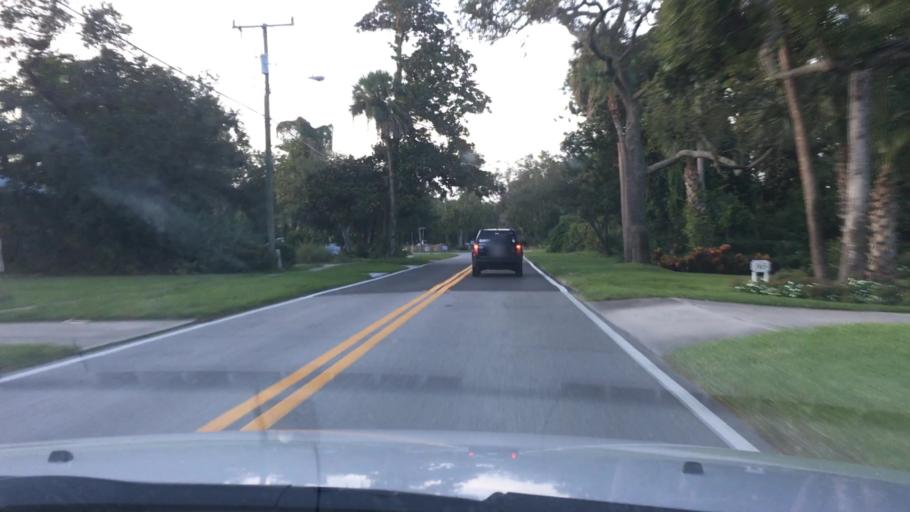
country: US
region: Florida
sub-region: Volusia County
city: Ormond Beach
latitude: 29.2952
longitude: -81.0599
